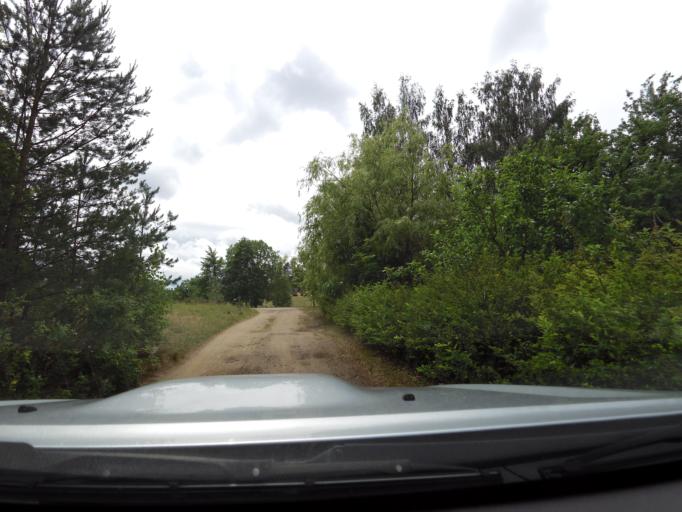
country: LT
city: Moletai
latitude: 55.3173
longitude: 25.5566
